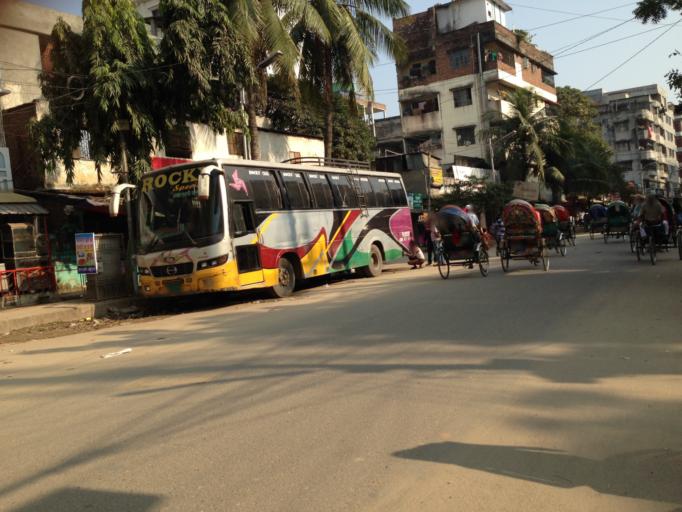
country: BD
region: Dhaka
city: Azimpur
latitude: 23.8020
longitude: 90.3493
